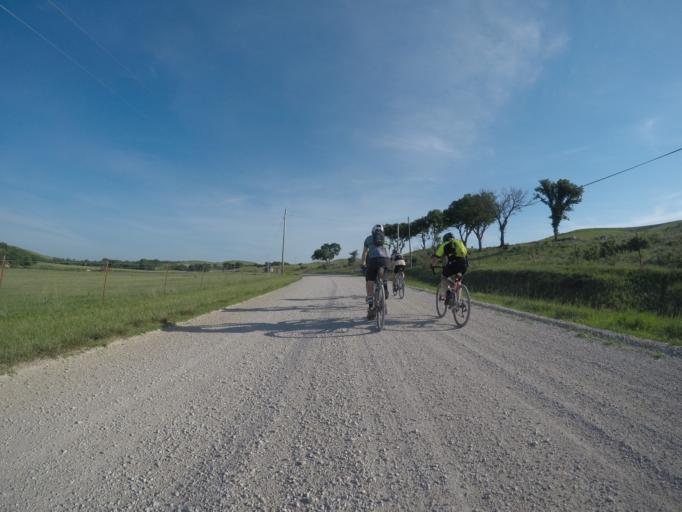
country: US
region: Kansas
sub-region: Riley County
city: Manhattan
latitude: 39.0629
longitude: -96.4995
